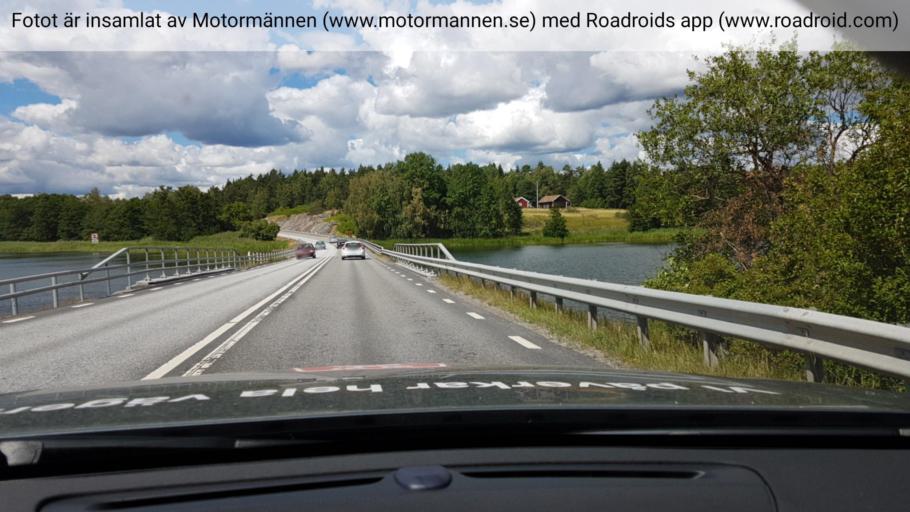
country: SE
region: Stockholm
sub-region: Vaxholms Kommun
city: Resaro
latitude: 59.4198
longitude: 18.3012
